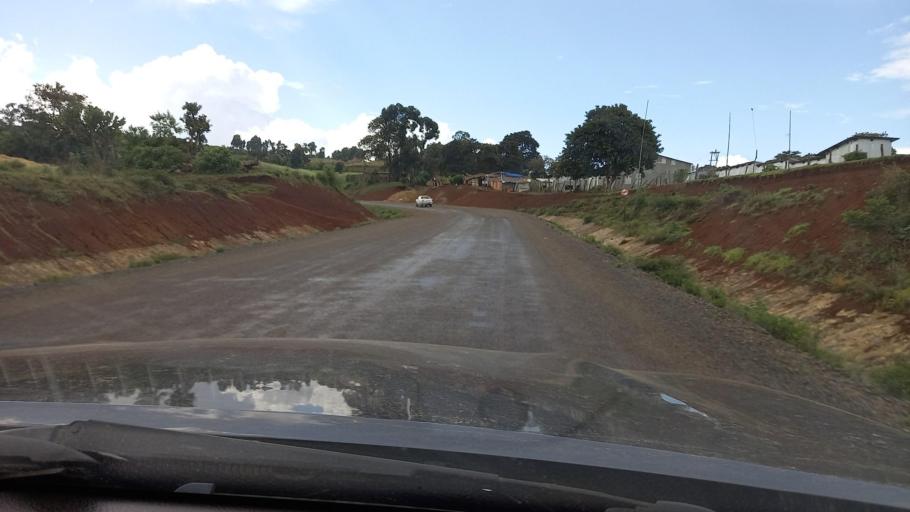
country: ET
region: Southern Nations, Nationalities, and People's Region
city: Mizan Teferi
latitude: 6.2141
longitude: 35.6401
